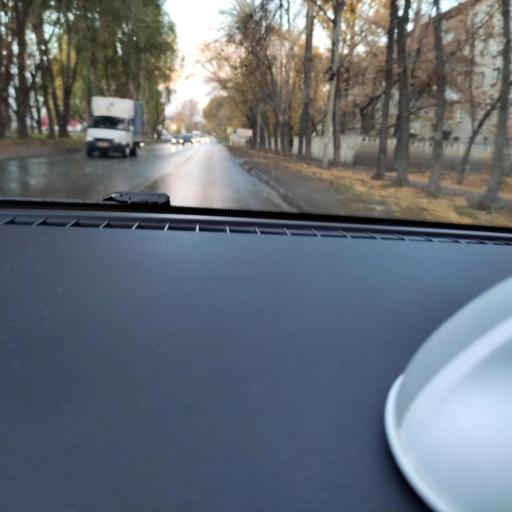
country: RU
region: Samara
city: Petra-Dubrava
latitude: 53.2308
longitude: 50.2919
